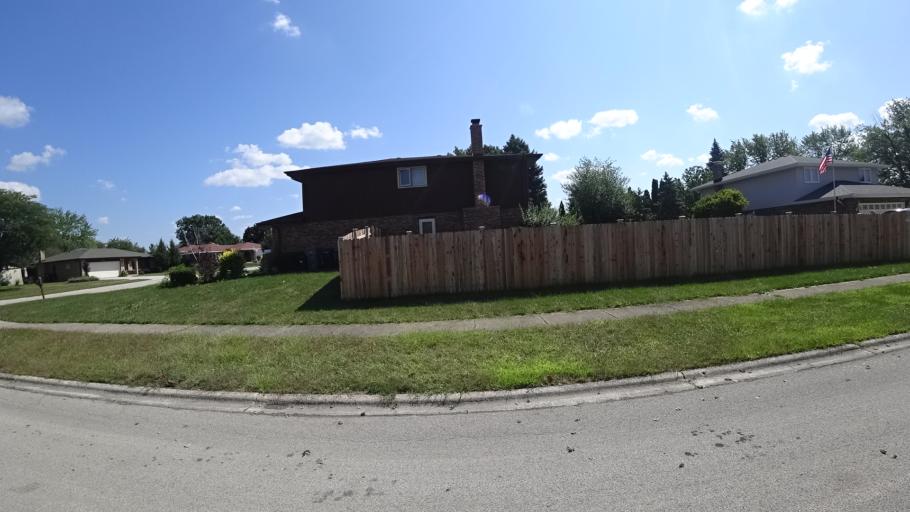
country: US
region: Illinois
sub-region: Cook County
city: Orland Park
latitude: 41.6338
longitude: -87.8428
